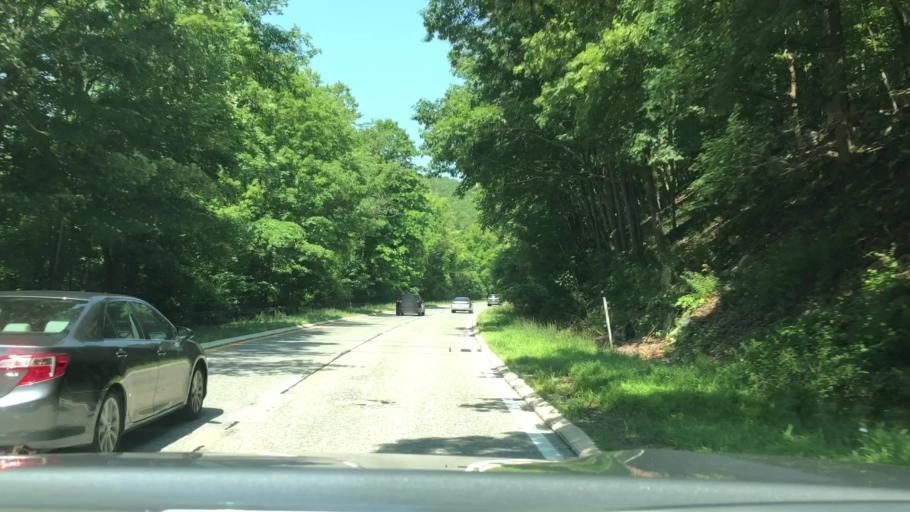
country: US
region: New York
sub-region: Rockland County
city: Thiells
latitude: 41.2503
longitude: -74.0405
